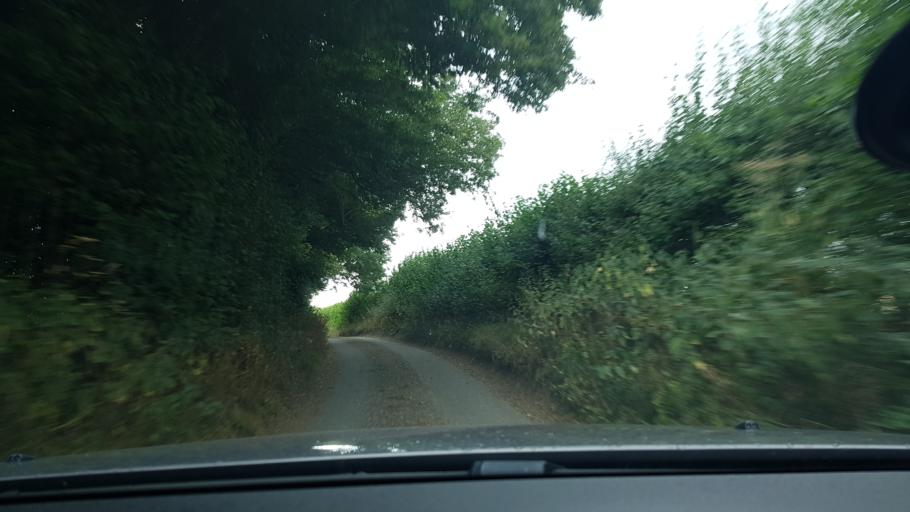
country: GB
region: England
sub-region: West Berkshire
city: Wickham
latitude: 51.4345
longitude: -1.4459
